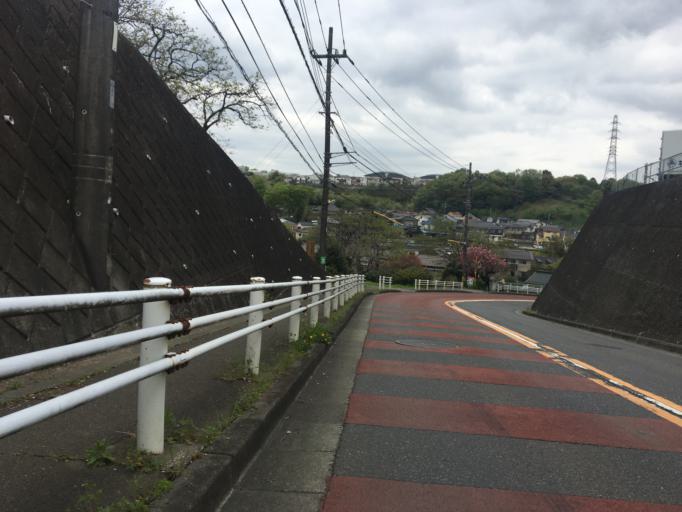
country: JP
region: Tokyo
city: Chofugaoka
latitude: 35.6261
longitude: 139.4867
